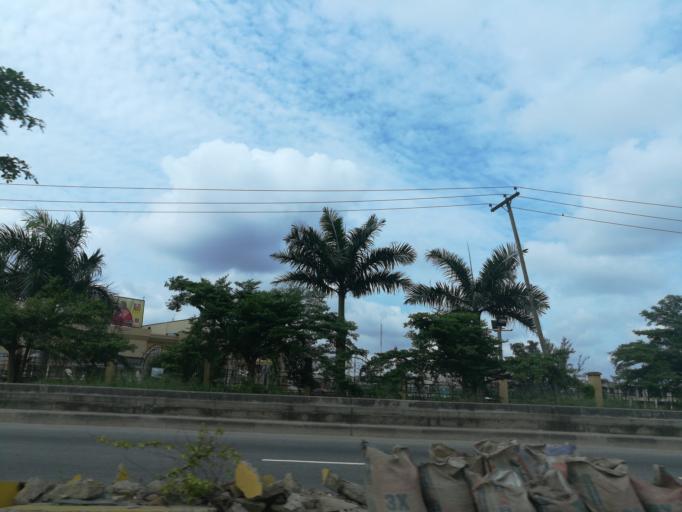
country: NG
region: Lagos
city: Somolu
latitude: 6.5545
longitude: 3.3726
